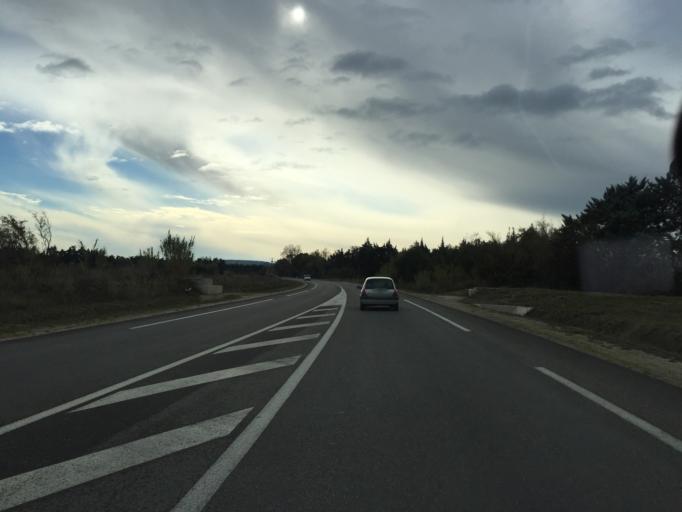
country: FR
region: Provence-Alpes-Cote d'Azur
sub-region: Departement du Vaucluse
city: L'Isle-sur-la-Sorgue
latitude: 43.8931
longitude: 5.0435
